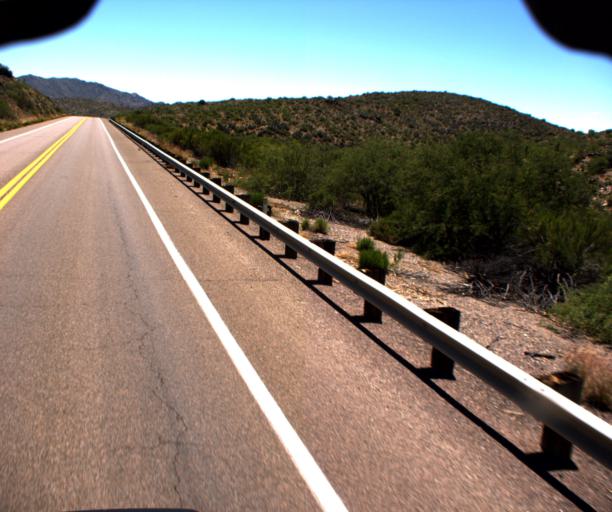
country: US
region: Arizona
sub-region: Yavapai County
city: Bagdad
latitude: 34.5463
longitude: -113.1478
